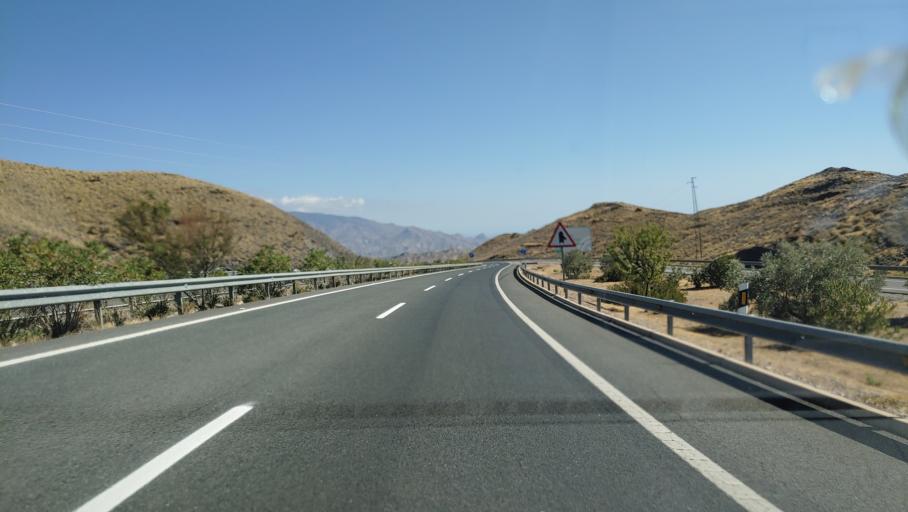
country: ES
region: Andalusia
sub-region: Provincia de Almeria
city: Gergal
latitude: 37.0910
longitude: -2.5235
